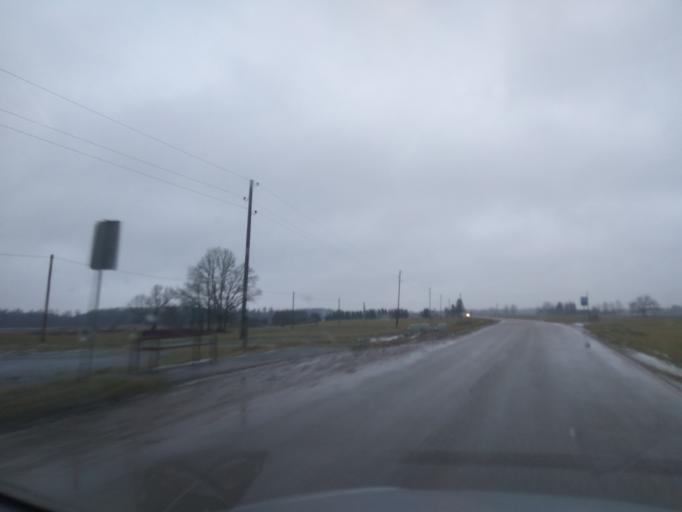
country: LV
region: Saldus Rajons
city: Saldus
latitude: 56.8358
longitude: 22.3780
